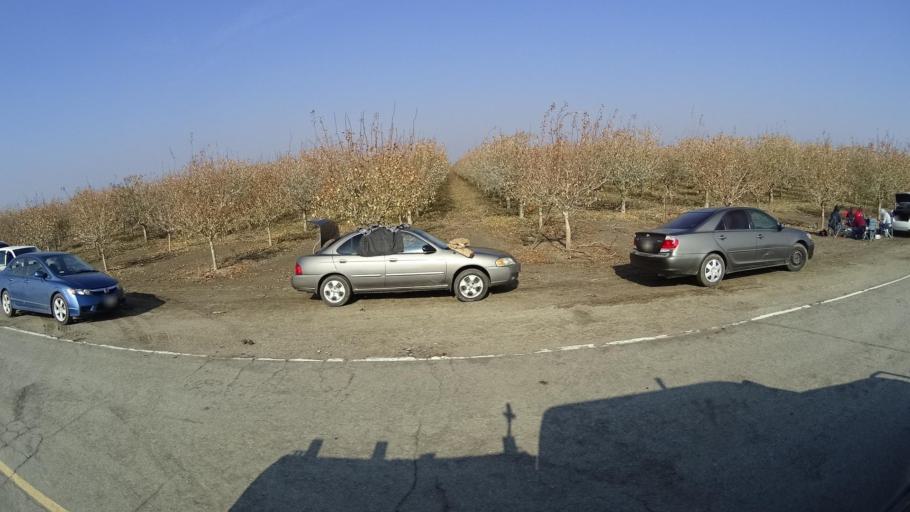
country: US
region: California
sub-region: Kern County
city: Buttonwillow
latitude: 35.3403
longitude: -119.3919
